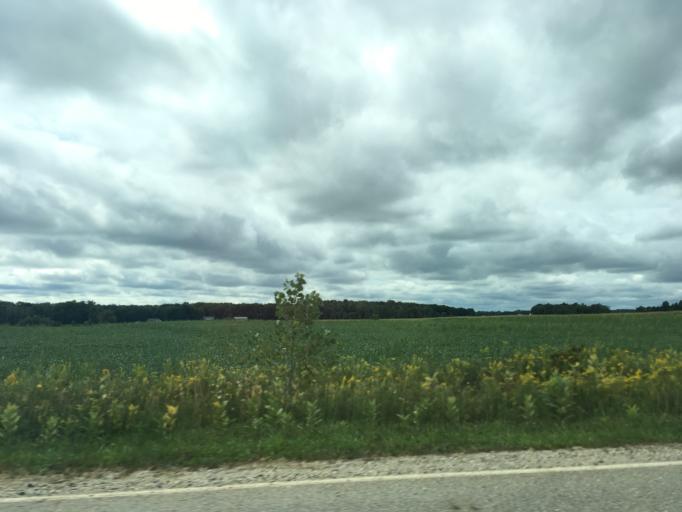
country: US
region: Michigan
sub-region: Lapeer County
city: Barnes Lake-Millers Lake
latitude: 43.3363
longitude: -83.3119
